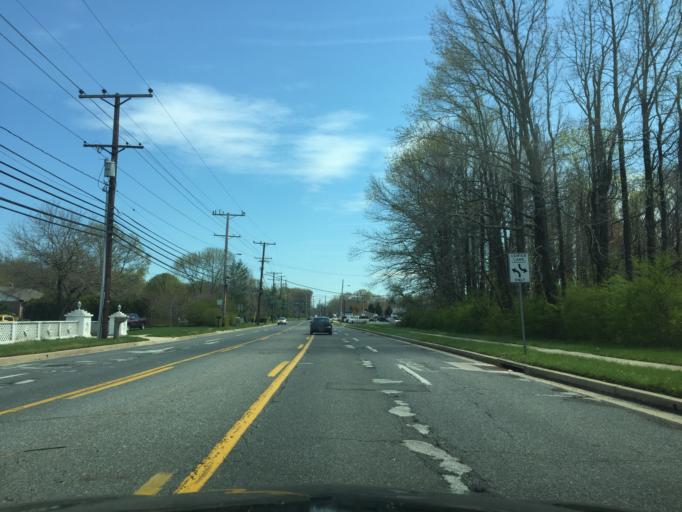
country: US
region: Maryland
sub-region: Baltimore County
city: Middle River
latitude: 39.3019
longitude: -76.4387
